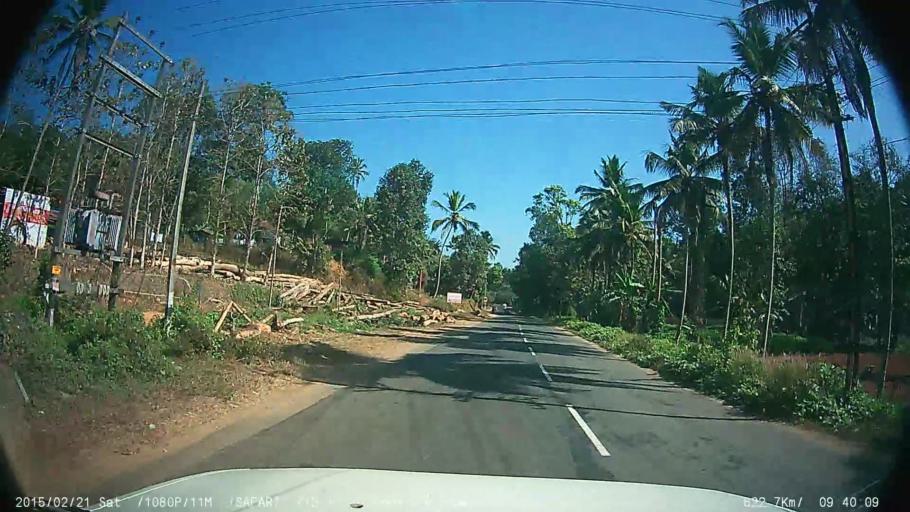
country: IN
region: Kerala
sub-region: Kottayam
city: Palackattumala
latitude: 9.7857
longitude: 76.5776
